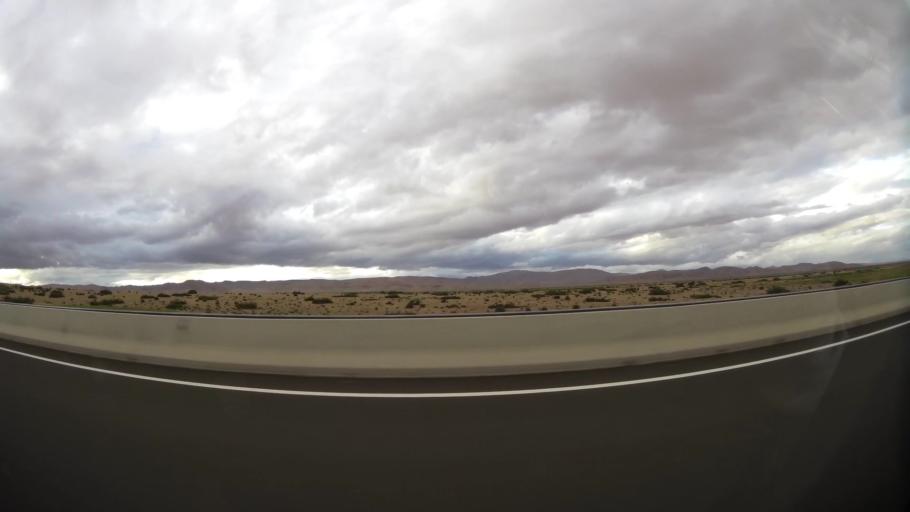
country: MA
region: Taza-Al Hoceima-Taounate
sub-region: Taza
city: Guercif
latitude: 34.3049
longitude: -3.6309
